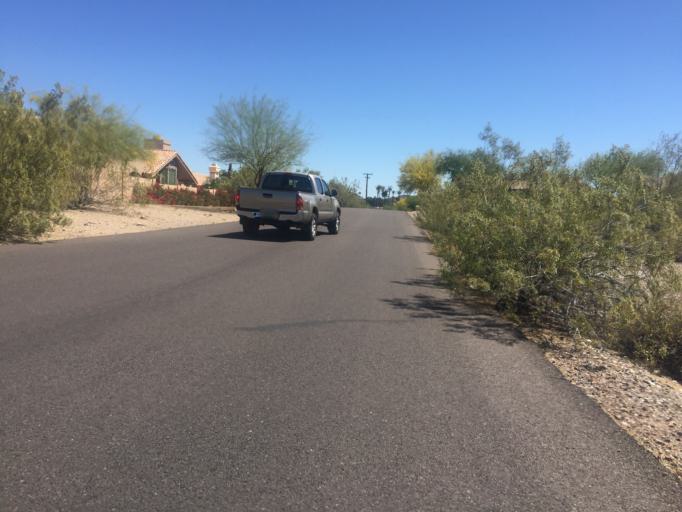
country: US
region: Arizona
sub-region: Maricopa County
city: Paradise Valley
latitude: 33.5720
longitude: -112.0281
